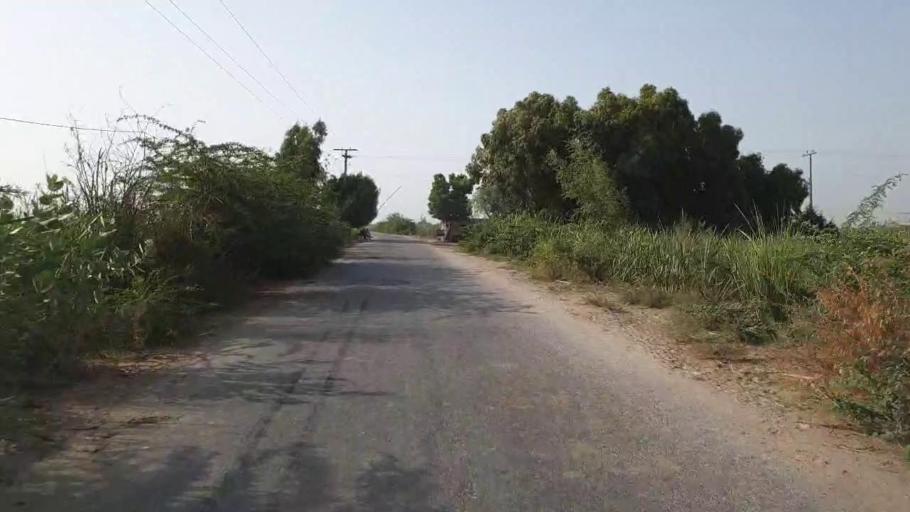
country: PK
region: Sindh
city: Jam Sahib
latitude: 26.4058
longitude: 68.8771
